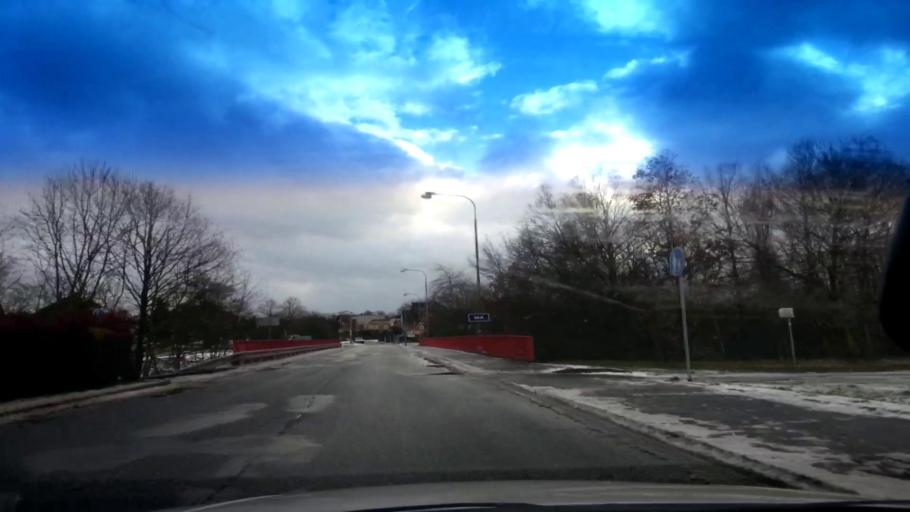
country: CZ
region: Karlovarsky
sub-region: Okres Cheb
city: Cheb
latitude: 50.0636
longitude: 12.3709
